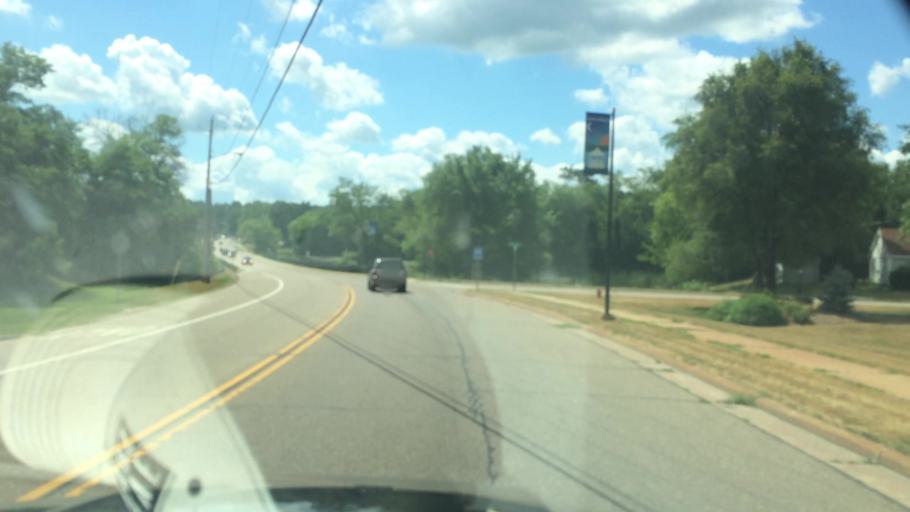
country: US
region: Wisconsin
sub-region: Waupaca County
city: Waupaca
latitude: 44.3459
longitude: -89.0721
